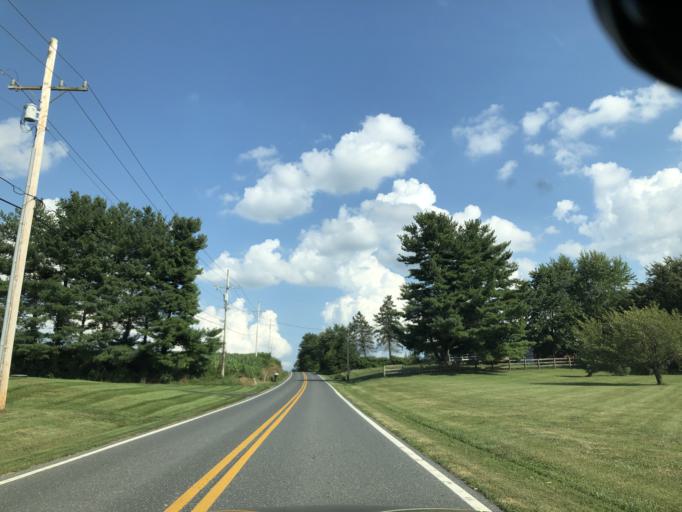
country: US
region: Maryland
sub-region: Frederick County
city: Linganore
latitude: 39.4722
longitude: -77.1808
